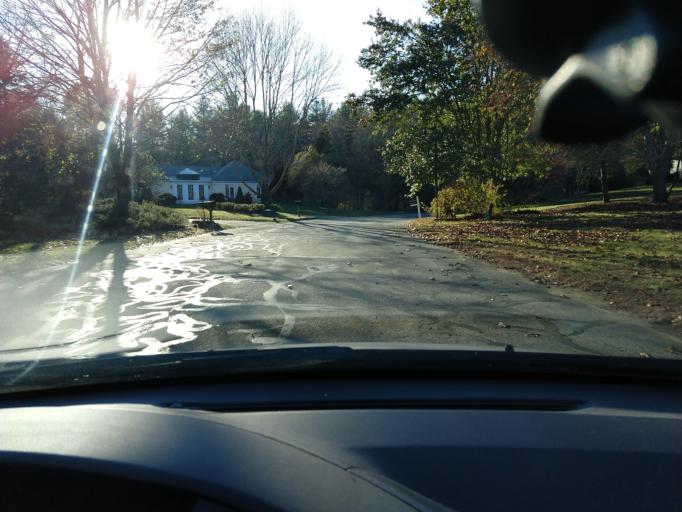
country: US
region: Massachusetts
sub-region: Middlesex County
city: Carlisle
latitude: 42.5003
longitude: -71.3240
